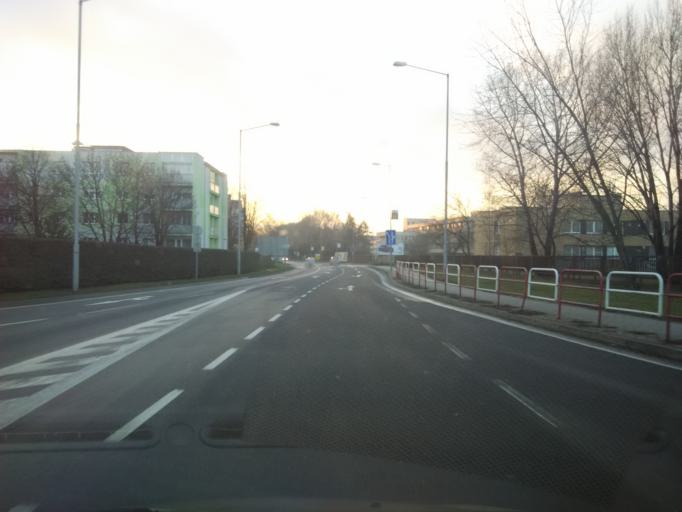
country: SK
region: Trnavsky
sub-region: Okres Trnava
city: Trnava
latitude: 48.3676
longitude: 17.5963
